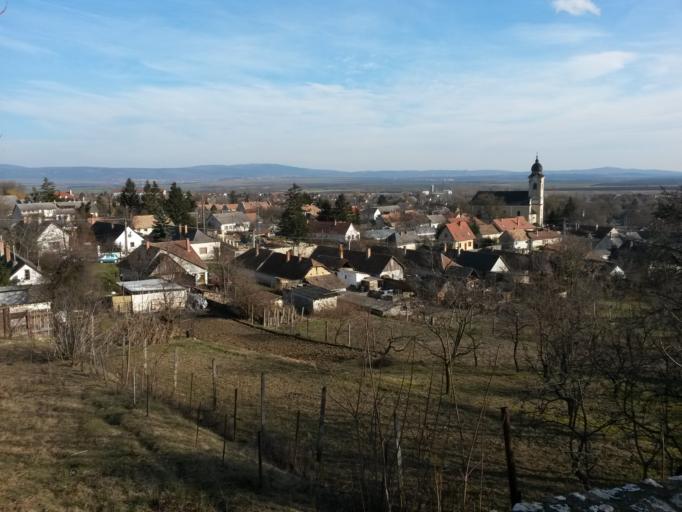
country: HU
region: Pest
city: Zsambek
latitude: 47.5497
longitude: 18.7157
